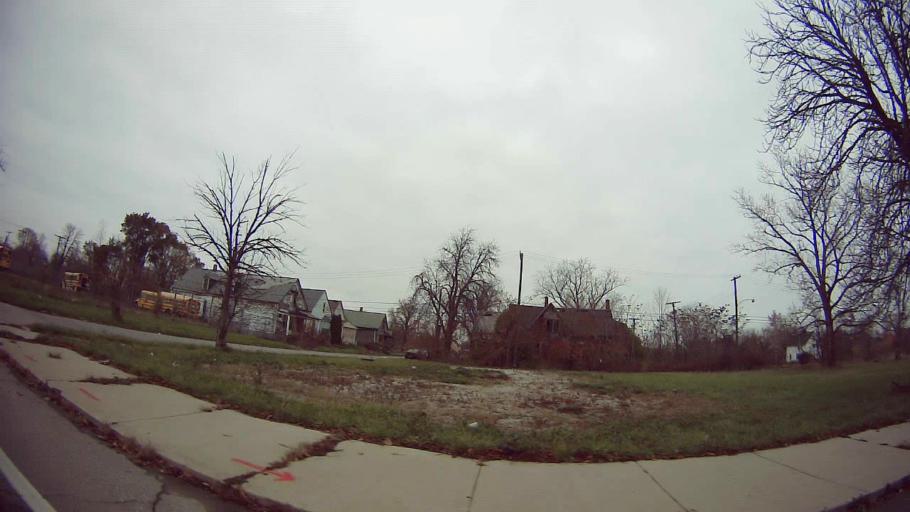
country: US
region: Michigan
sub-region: Wayne County
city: Hamtramck
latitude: 42.3650
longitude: -83.0447
